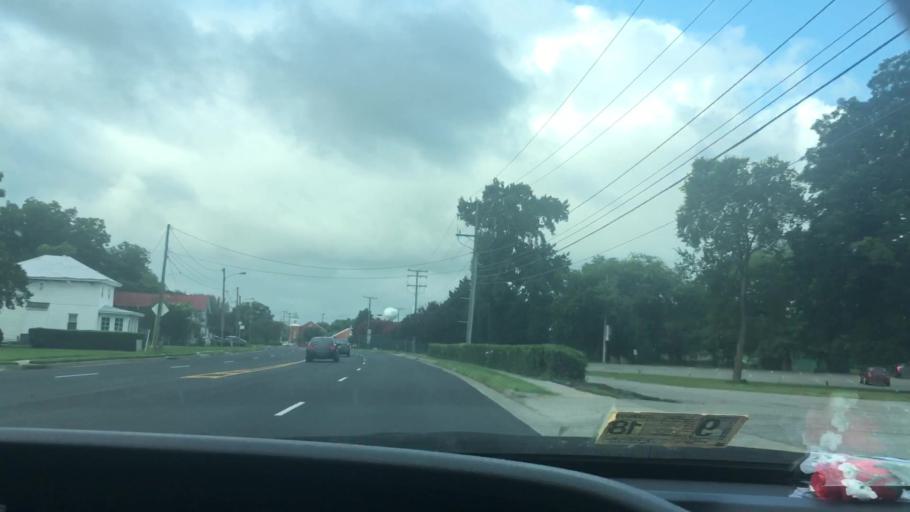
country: US
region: Virginia
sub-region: City of Hampton
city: East Hampton
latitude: 37.0255
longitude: -76.3250
